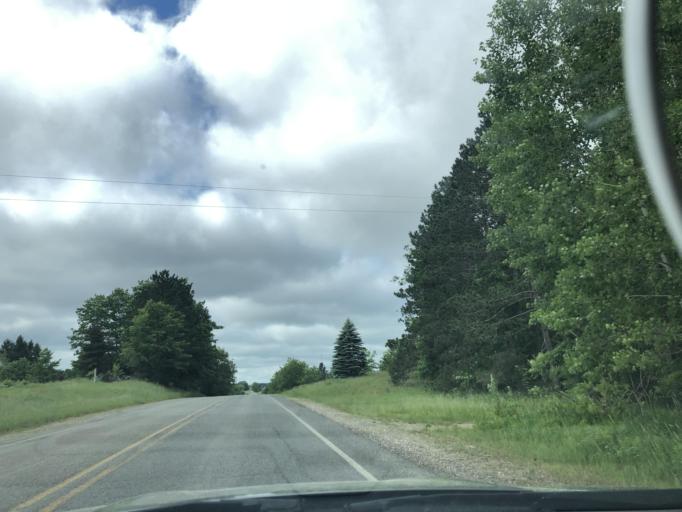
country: US
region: Michigan
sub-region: Missaukee County
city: Lake City
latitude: 44.4479
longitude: -85.2163
